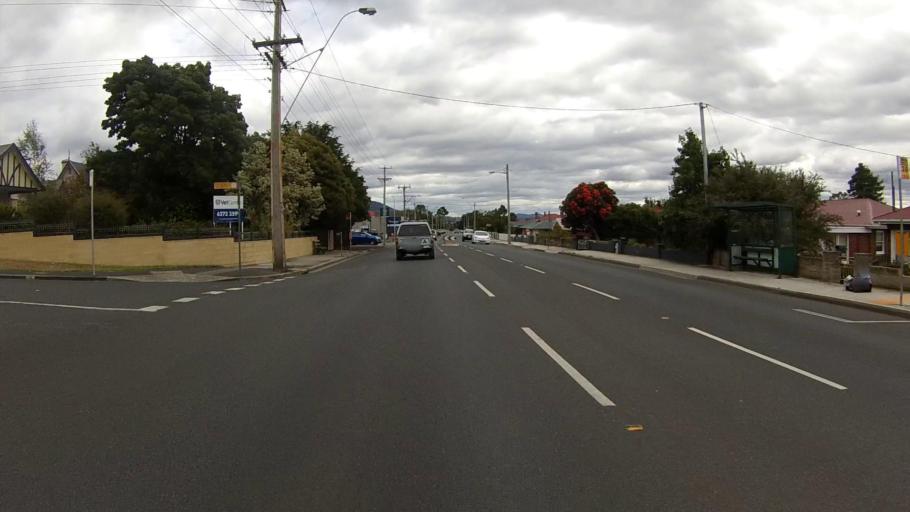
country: AU
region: Tasmania
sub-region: Glenorchy
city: Glenorchy
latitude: -42.8266
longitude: 147.2667
